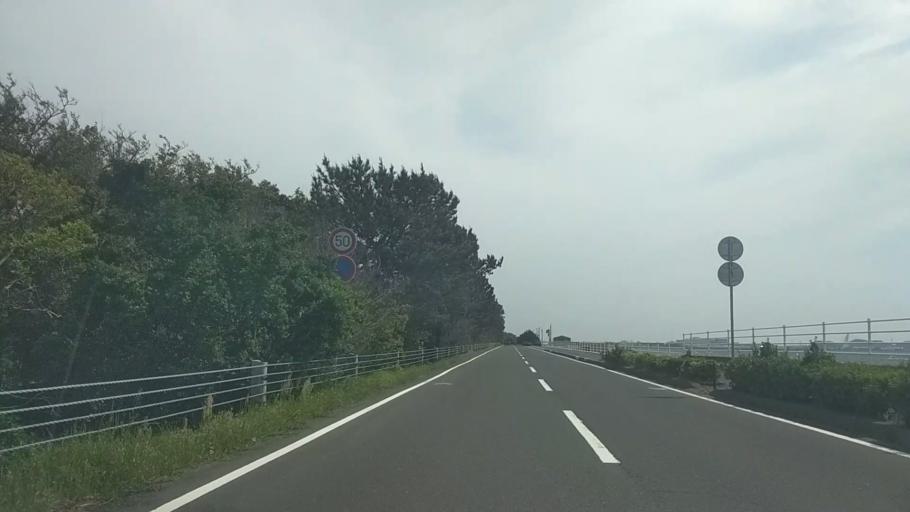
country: JP
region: Shizuoka
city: Kosai-shi
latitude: 34.7172
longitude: 137.5853
